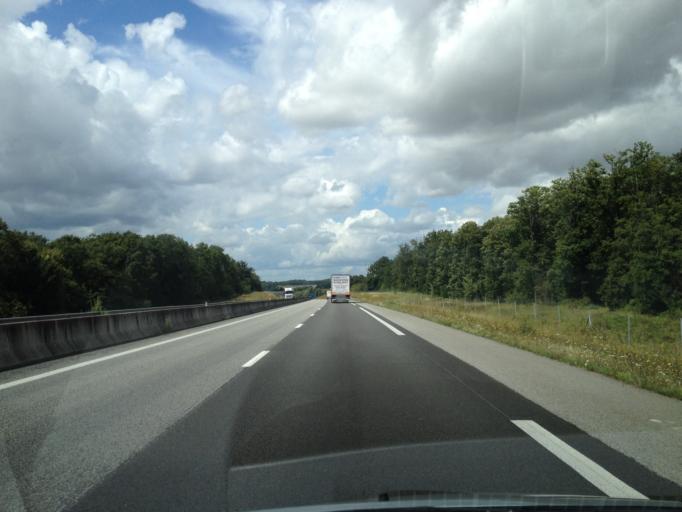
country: FR
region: Pays de la Loire
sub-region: Departement de la Sarthe
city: Champfleur
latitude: 48.3170
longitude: 0.1330
